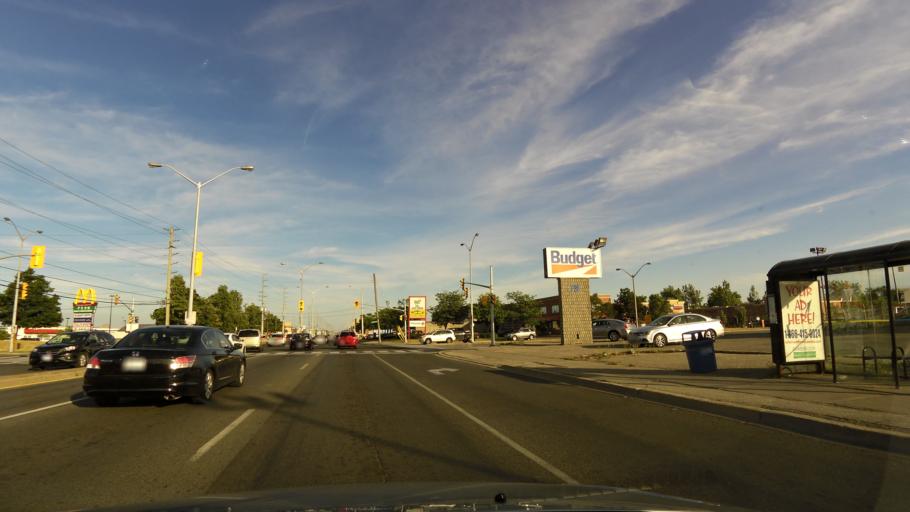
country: CA
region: Ontario
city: Brampton
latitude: 43.6900
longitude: -79.7420
